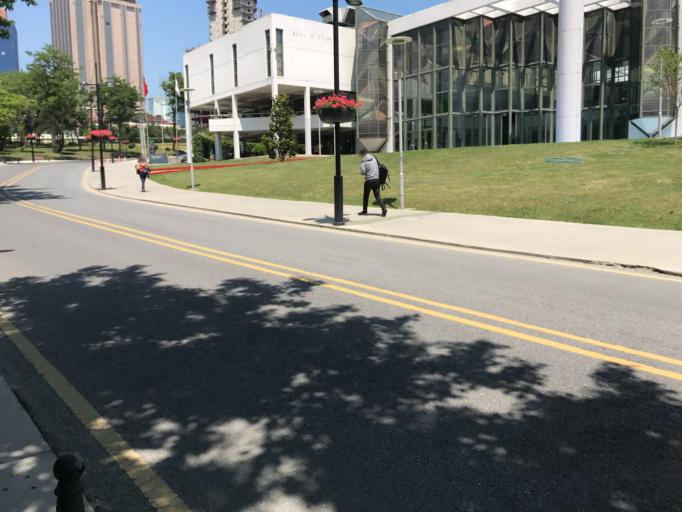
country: TR
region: Istanbul
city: Sisli
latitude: 41.1066
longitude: 29.0225
